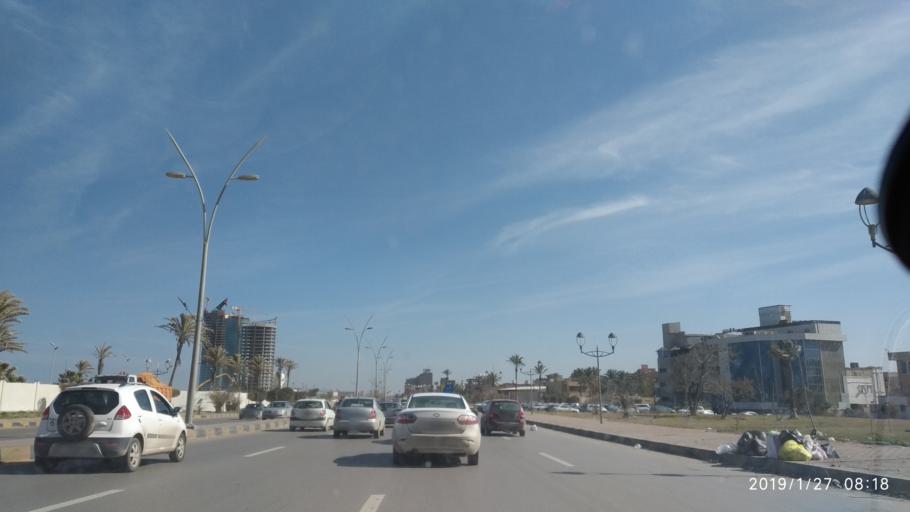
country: LY
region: Tripoli
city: Tripoli
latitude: 32.9066
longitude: 13.2573
